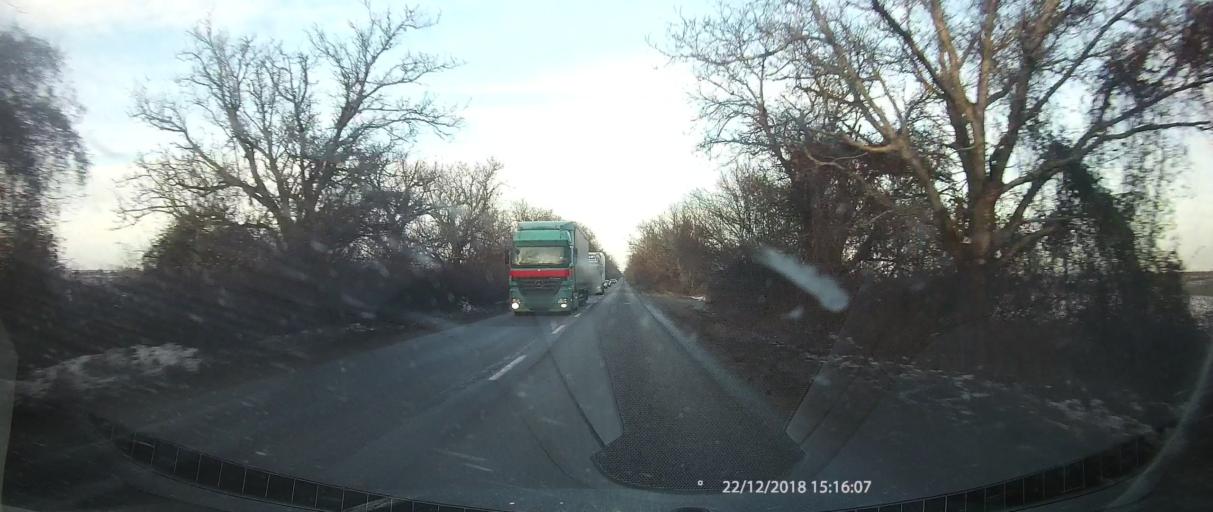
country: BG
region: Ruse
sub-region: Obshtina Dve Mogili
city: Dve Mogili
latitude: 43.6022
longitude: 25.8423
